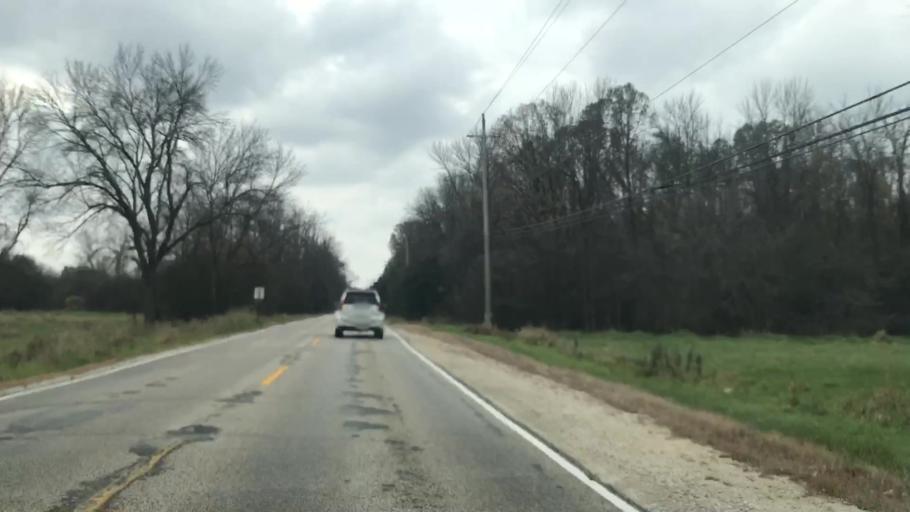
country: US
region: Wisconsin
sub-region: Waukesha County
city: Menomonee Falls
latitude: 43.2040
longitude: -88.1427
